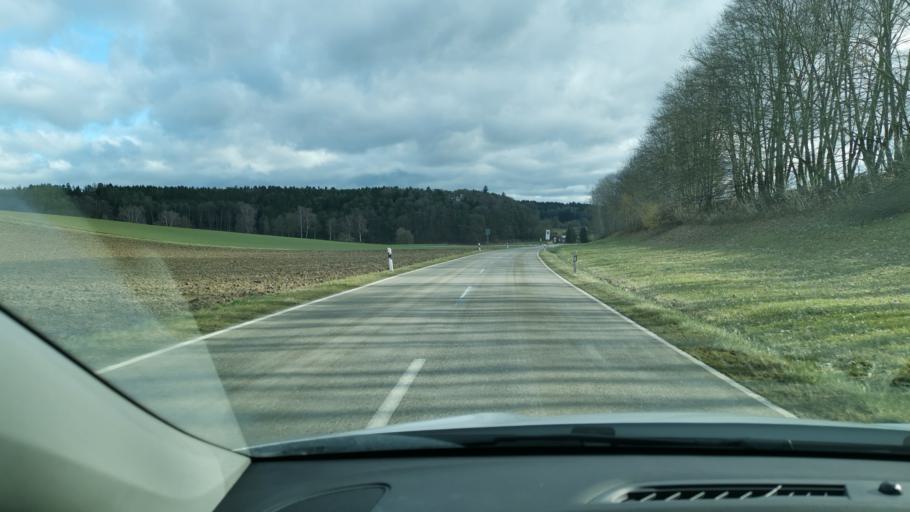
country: DE
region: Bavaria
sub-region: Swabia
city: Aindling
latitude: 48.5602
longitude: 10.9788
